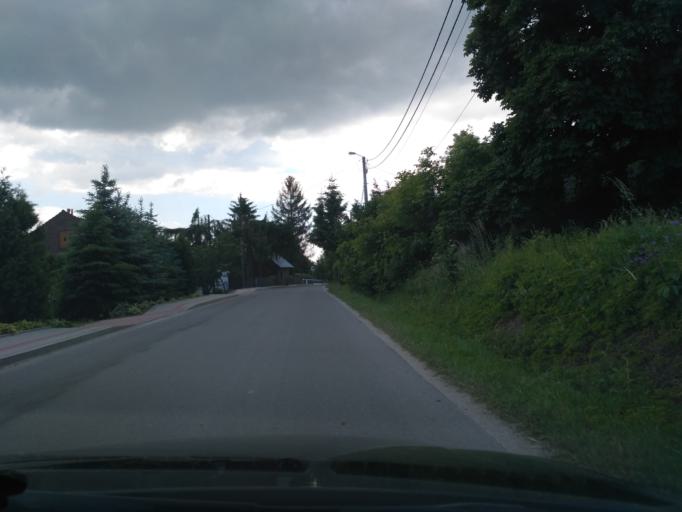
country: PL
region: Subcarpathian Voivodeship
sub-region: Powiat lancucki
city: Wysoka
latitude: 50.0507
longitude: 22.2591
